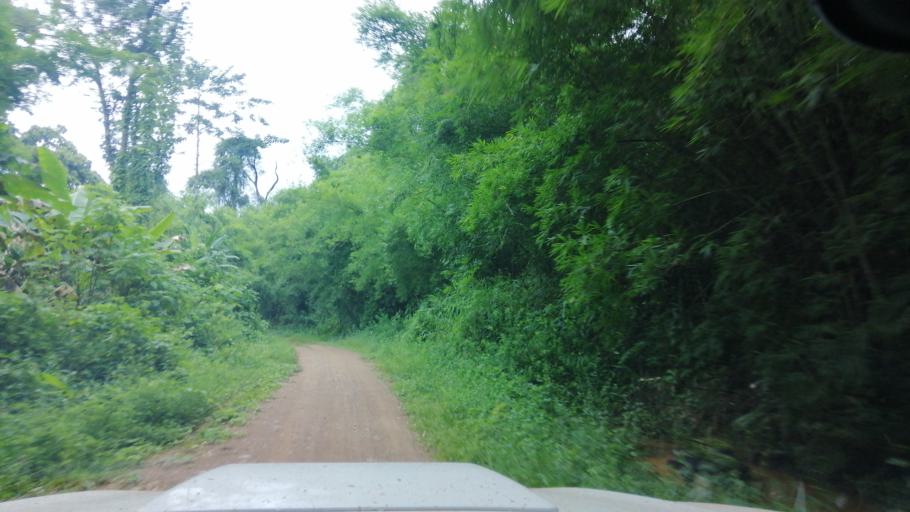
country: TH
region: Nan
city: Mae Charim
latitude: 18.7456
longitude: 101.2853
